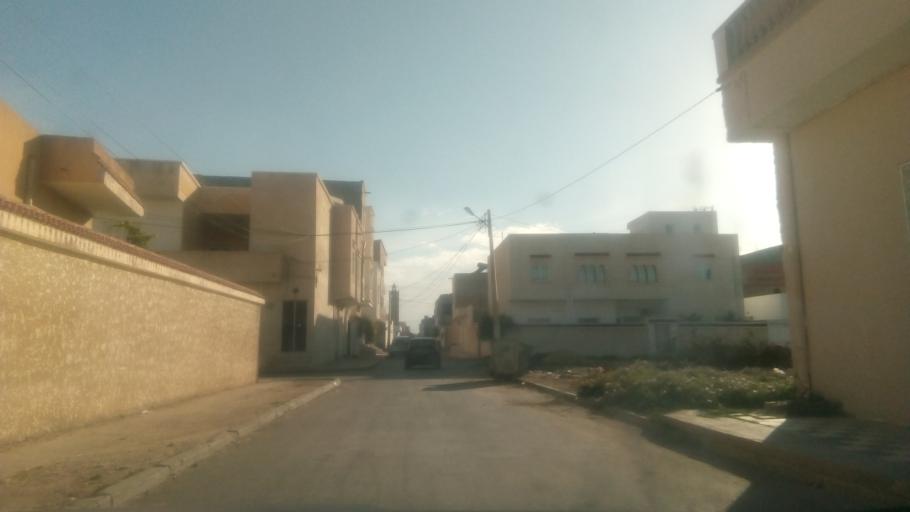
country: TN
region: Al Qayrawan
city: Kairouan
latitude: 35.6682
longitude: 10.0794
